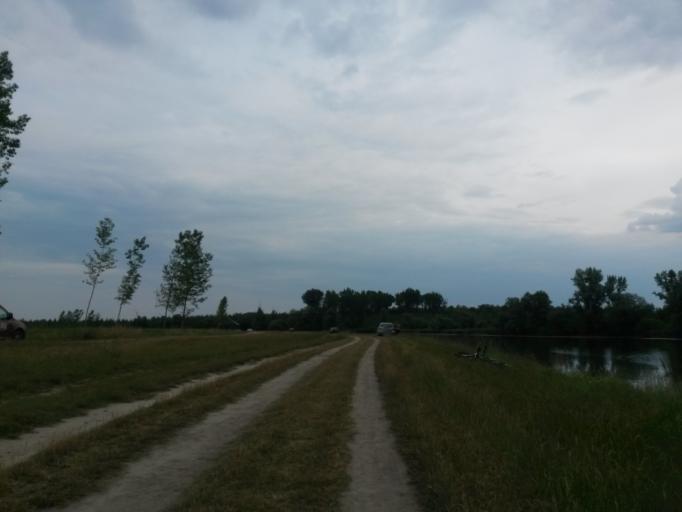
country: HR
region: Osjecko-Baranjska
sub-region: Grad Osijek
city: Bilje
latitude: 45.5887
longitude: 18.7431
